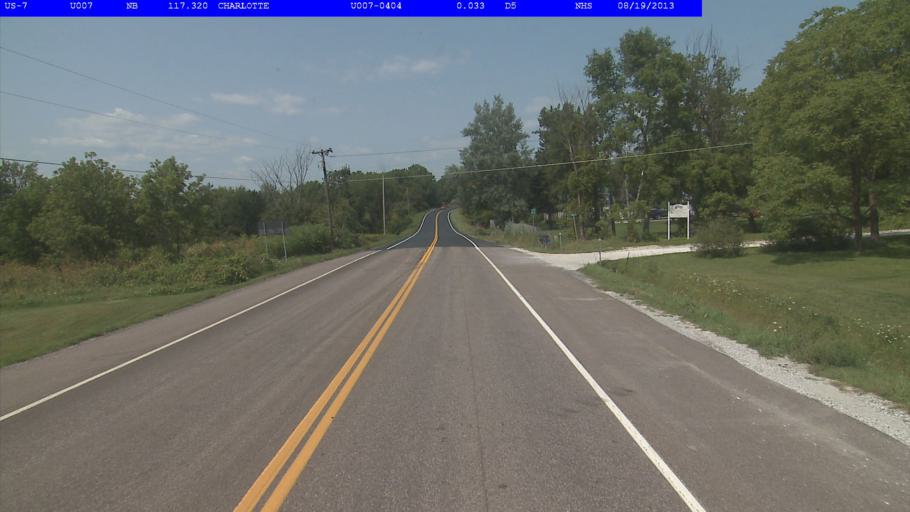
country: US
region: Vermont
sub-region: Addison County
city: Vergennes
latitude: 44.2630
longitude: -73.2306
